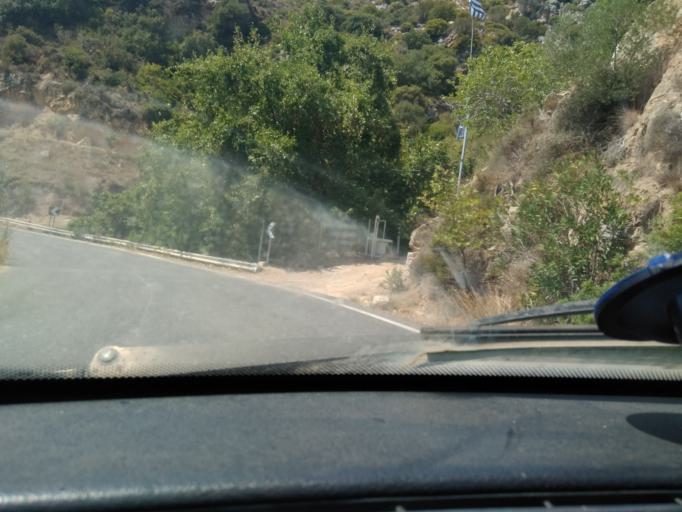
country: GR
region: Crete
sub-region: Nomos Lasithiou
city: Siteia
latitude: 35.1298
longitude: 26.0661
